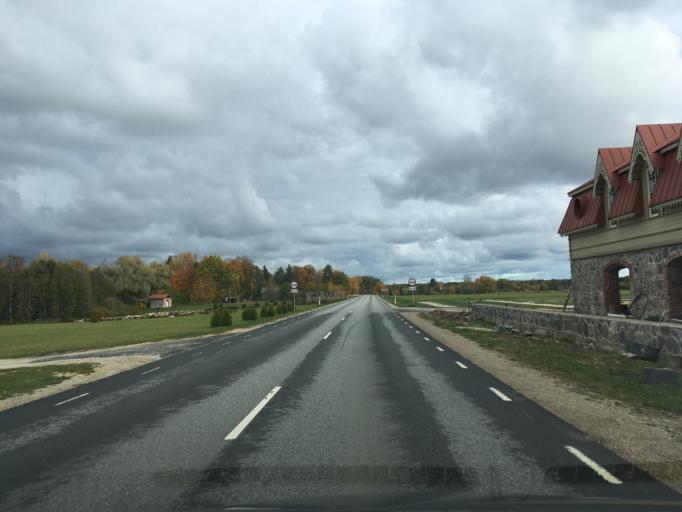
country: EE
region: Harju
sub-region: Anija vald
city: Kehra
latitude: 59.2789
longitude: 25.3691
